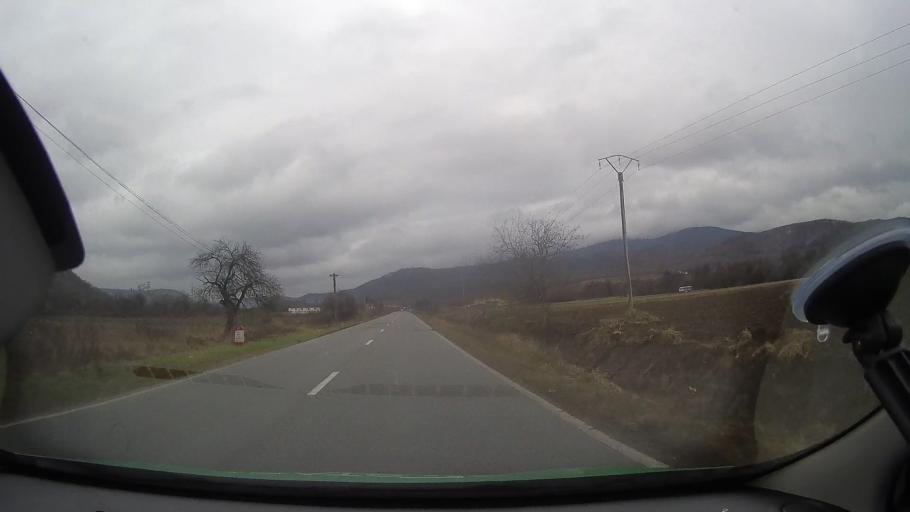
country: RO
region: Arad
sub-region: Comuna Buteni
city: Buteni
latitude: 46.3140
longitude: 22.1399
